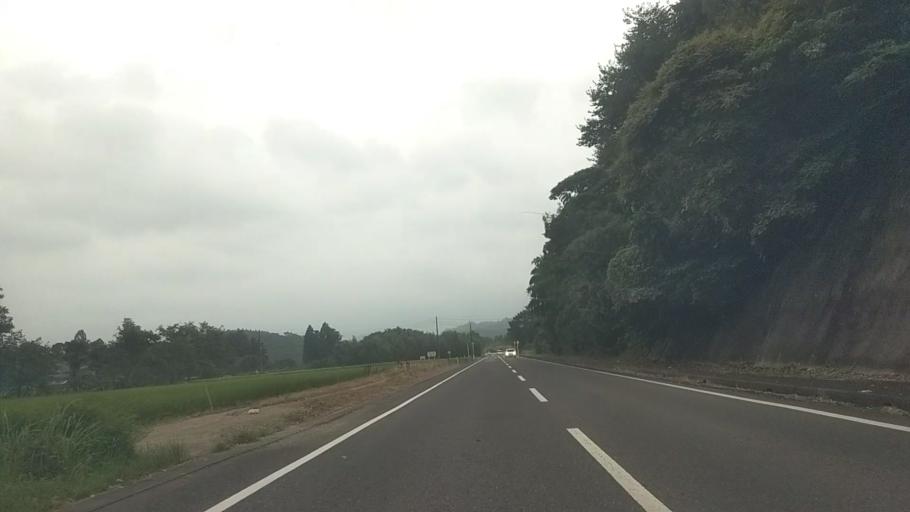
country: JP
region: Chiba
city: Kimitsu
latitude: 35.2197
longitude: 139.9152
